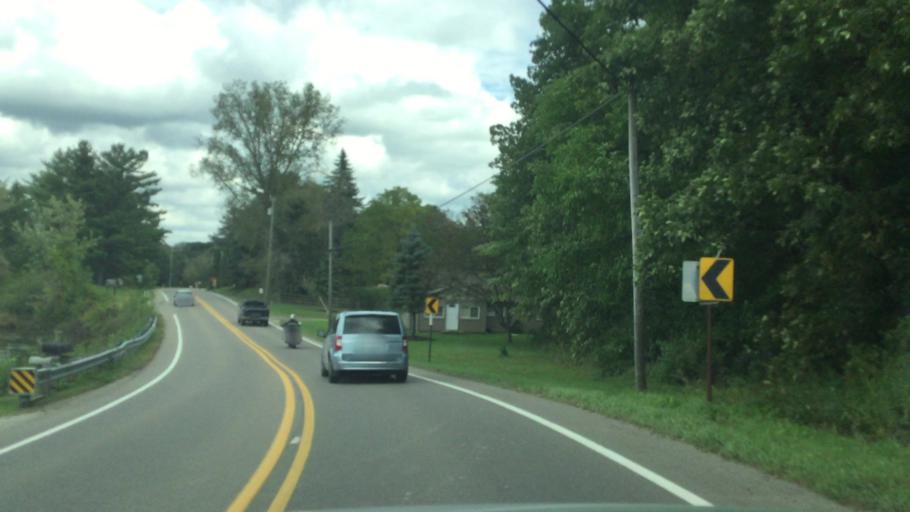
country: US
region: Michigan
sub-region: Livingston County
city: Brighton
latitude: 42.5502
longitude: -83.7748
